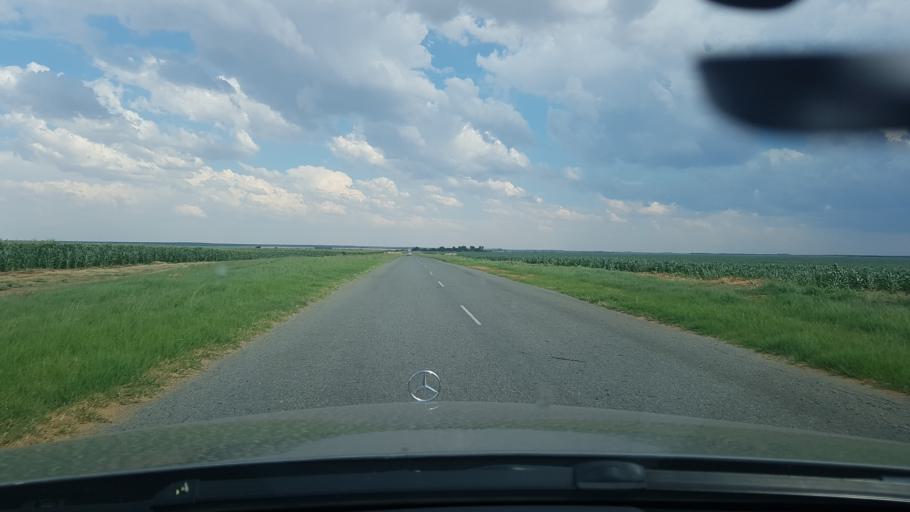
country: ZA
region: North-West
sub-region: Dr Ruth Segomotsi Mompati District Municipality
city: Bloemhof
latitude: -27.8179
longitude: 25.6294
